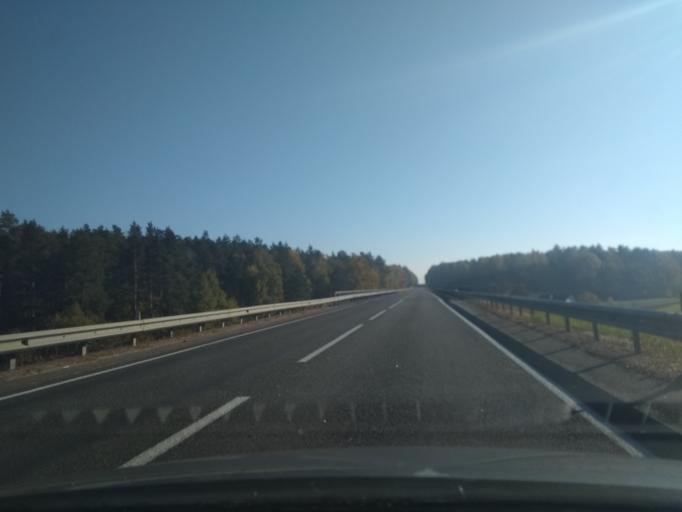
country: BY
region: Grodnenskaya
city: Zel'va
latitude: 53.1392
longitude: 24.9224
